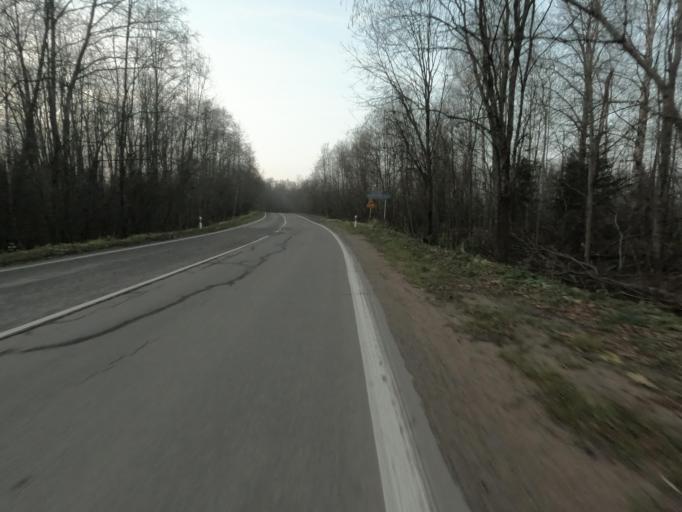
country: RU
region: Leningrad
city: Kirovsk
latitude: 59.8573
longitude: 30.9869
